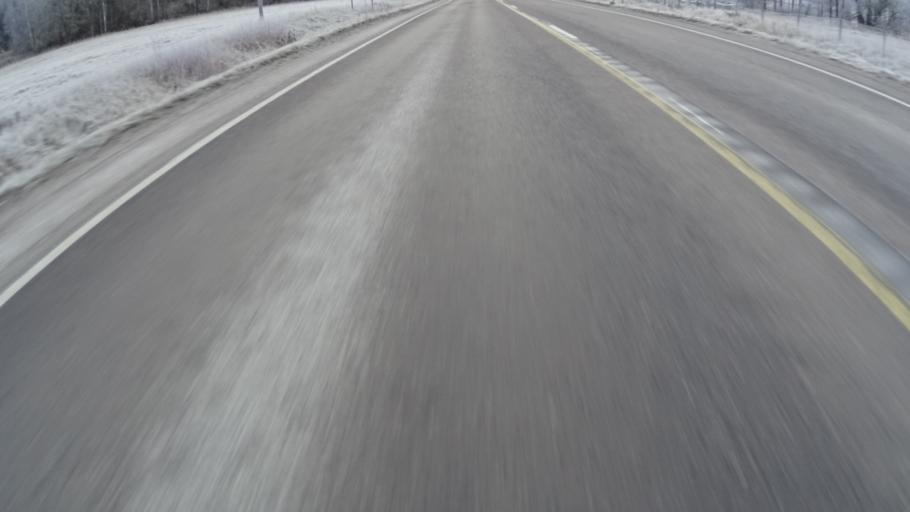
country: FI
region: Uusimaa
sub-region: Helsinki
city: Nurmijaervi
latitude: 60.4286
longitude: 24.7248
